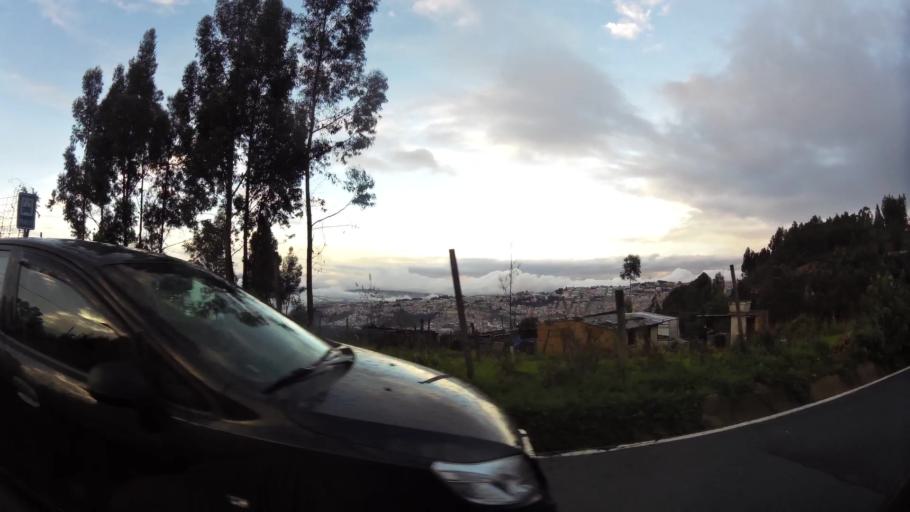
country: EC
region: Pichincha
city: Quito
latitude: -0.1112
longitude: -78.5167
